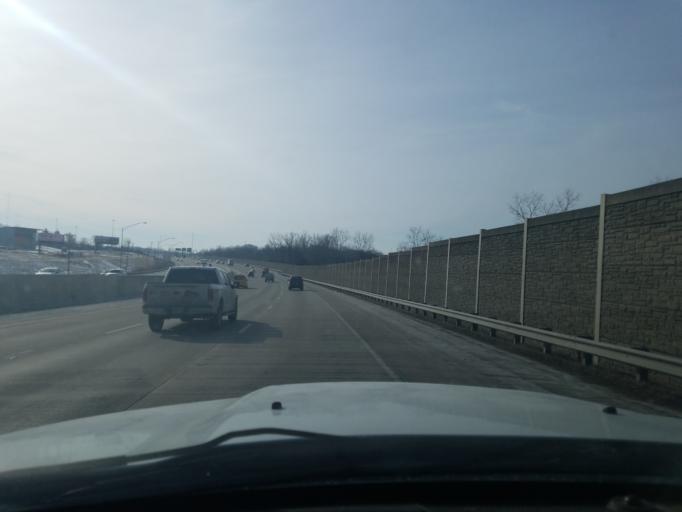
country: US
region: Indiana
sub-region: Allen County
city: Fort Wayne
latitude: 41.1282
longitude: -85.1781
